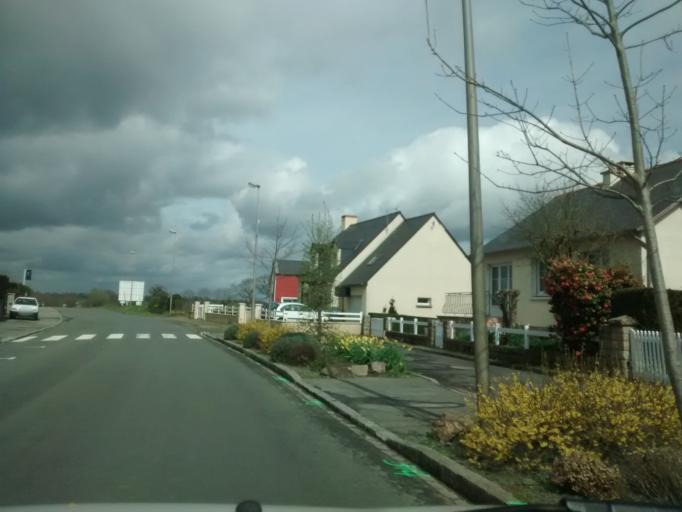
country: FR
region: Brittany
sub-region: Departement d'Ille-et-Vilaine
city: Livre-sur-Changeon
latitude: 48.2219
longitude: -1.3468
